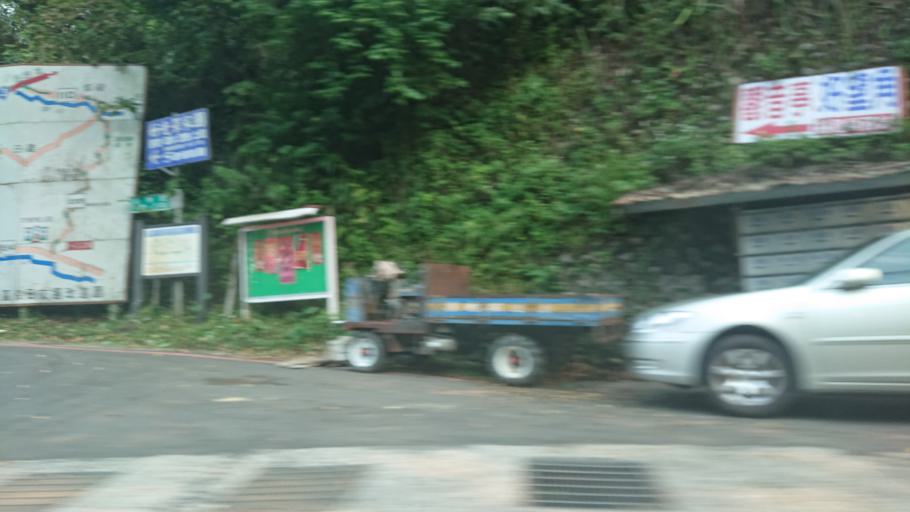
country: TW
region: Taiwan
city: Daxi
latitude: 24.8704
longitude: 121.4086
